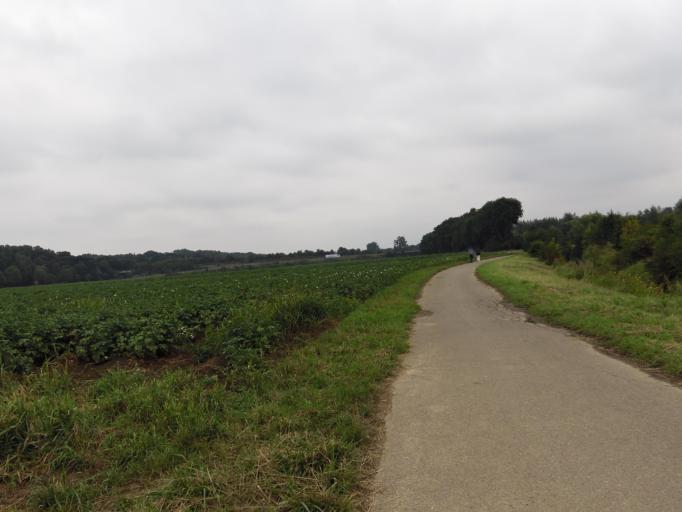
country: DE
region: North Rhine-Westphalia
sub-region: Regierungsbezirk Koln
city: Ubach-Palenberg
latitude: 50.9506
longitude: 6.1049
